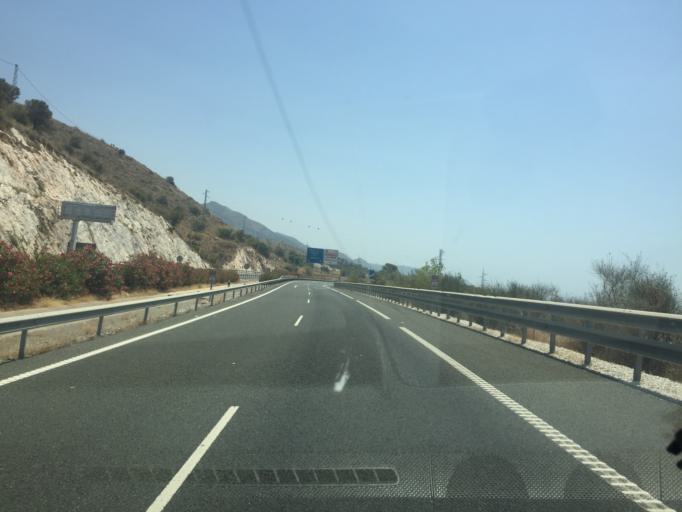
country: ES
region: Andalusia
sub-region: Provincia de Malaga
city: Nerja
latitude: 36.7643
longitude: -3.8594
